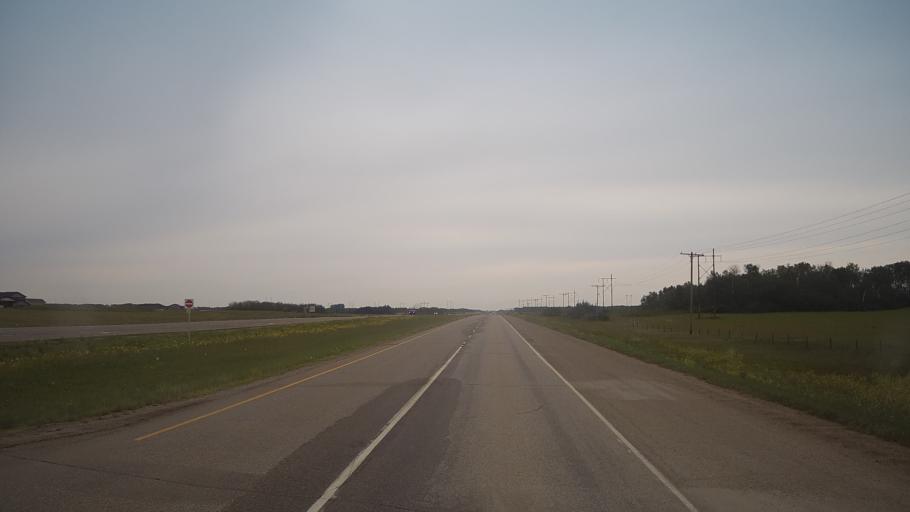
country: CA
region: Saskatchewan
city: Saskatoon
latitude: 51.9402
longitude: -106.5396
